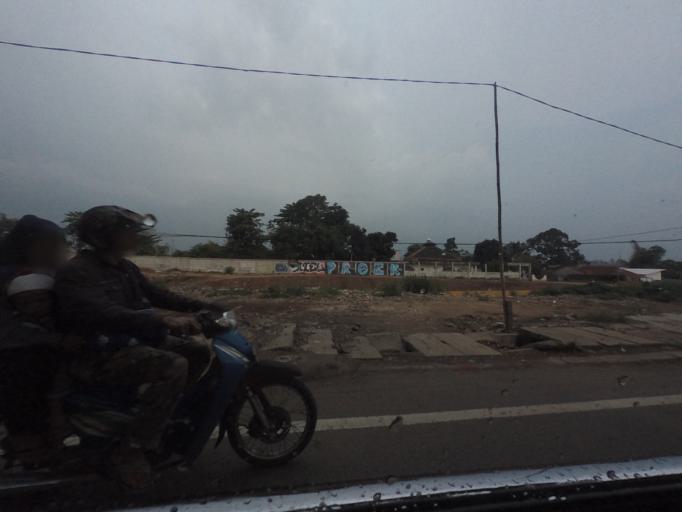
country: ID
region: West Java
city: Cicurug
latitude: -6.7545
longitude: 106.7994
